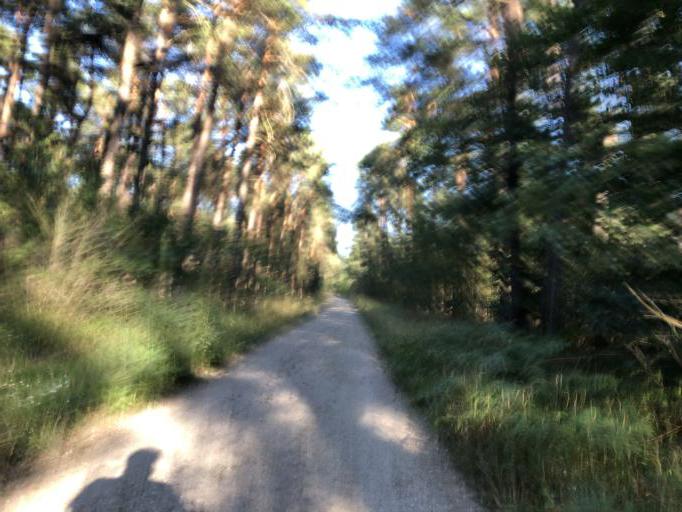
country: DE
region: Bavaria
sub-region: Regierungsbezirk Mittelfranken
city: Buckenhof
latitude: 49.5440
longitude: 11.0660
